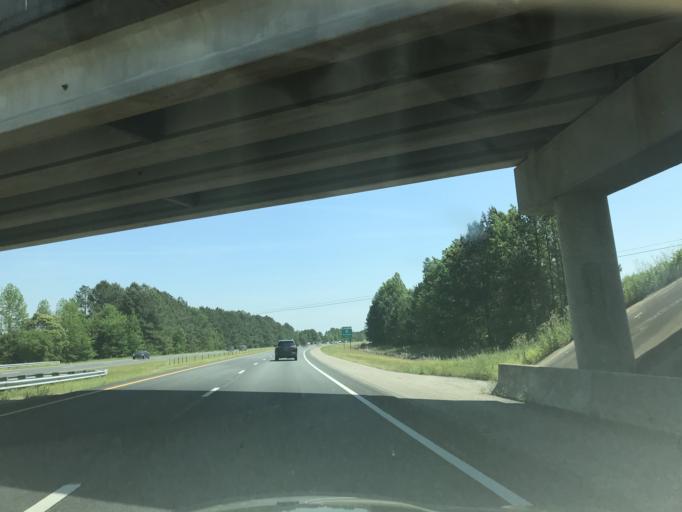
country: US
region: North Carolina
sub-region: Johnston County
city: Benson
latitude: 35.3412
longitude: -78.4664
